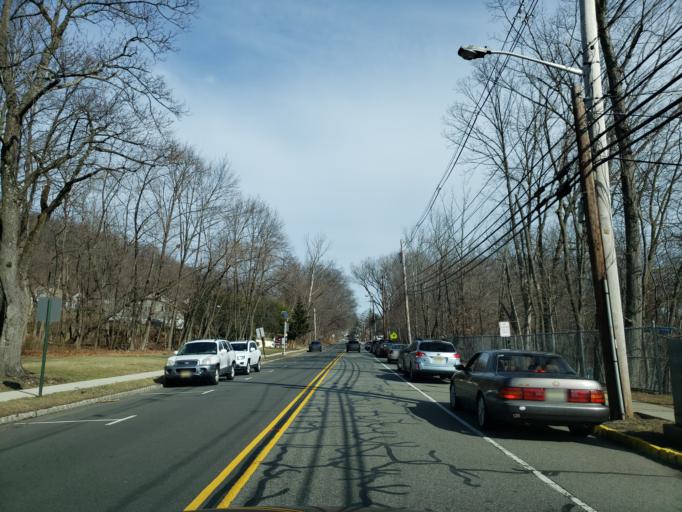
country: US
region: New Jersey
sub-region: Essex County
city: Verona
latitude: 40.8421
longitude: -74.2482
